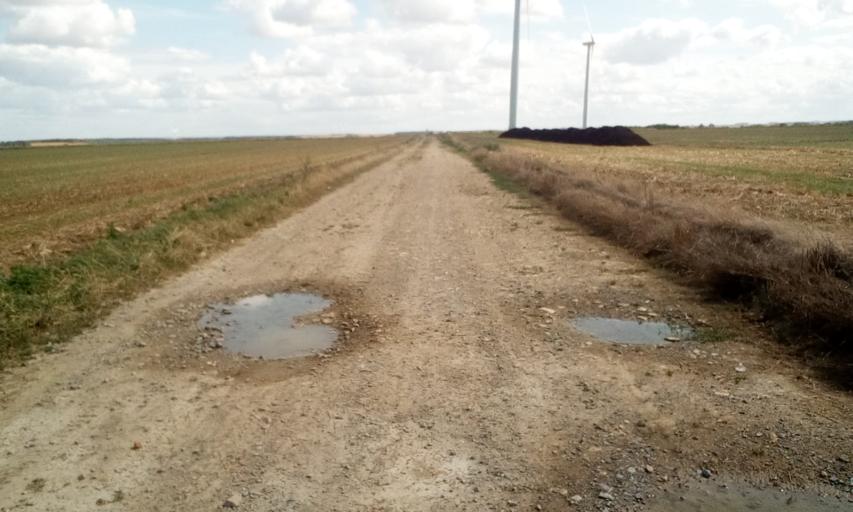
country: FR
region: Lower Normandy
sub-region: Departement du Calvados
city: Bellengreville
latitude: 49.0981
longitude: -0.2280
